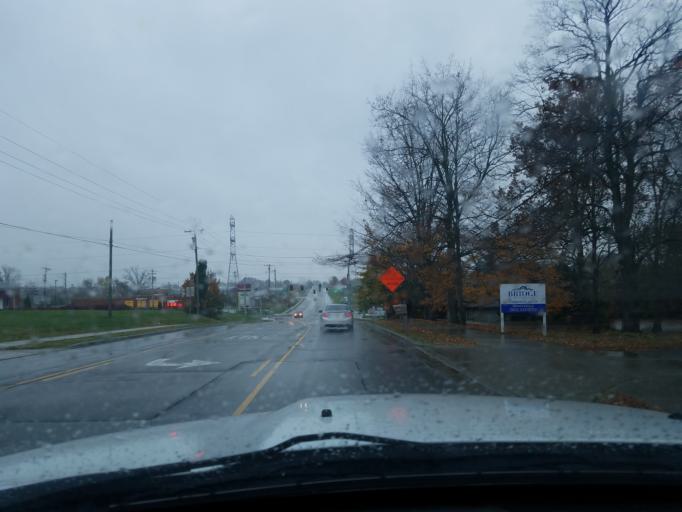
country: US
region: Indiana
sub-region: Floyd County
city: New Albany
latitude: 38.3240
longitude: -85.8197
